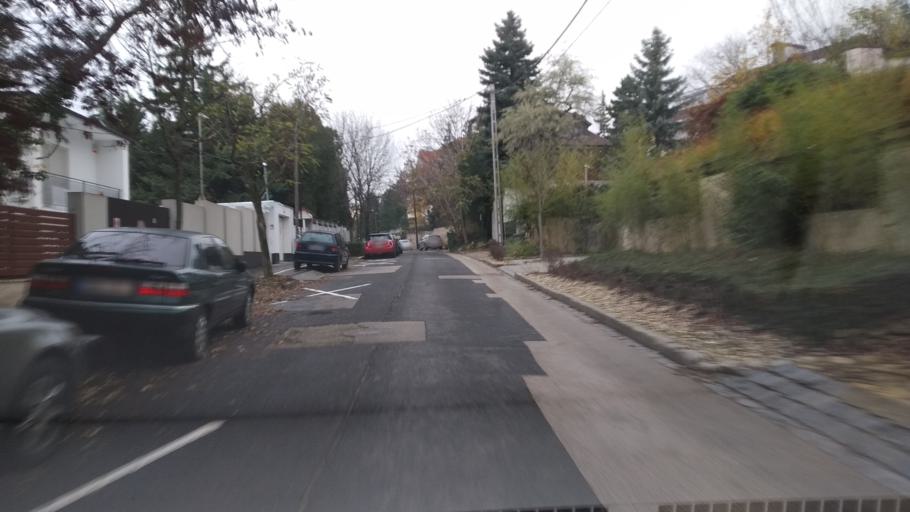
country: HU
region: Budapest
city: Budapest II. keruelet
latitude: 47.5215
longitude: 19.0108
